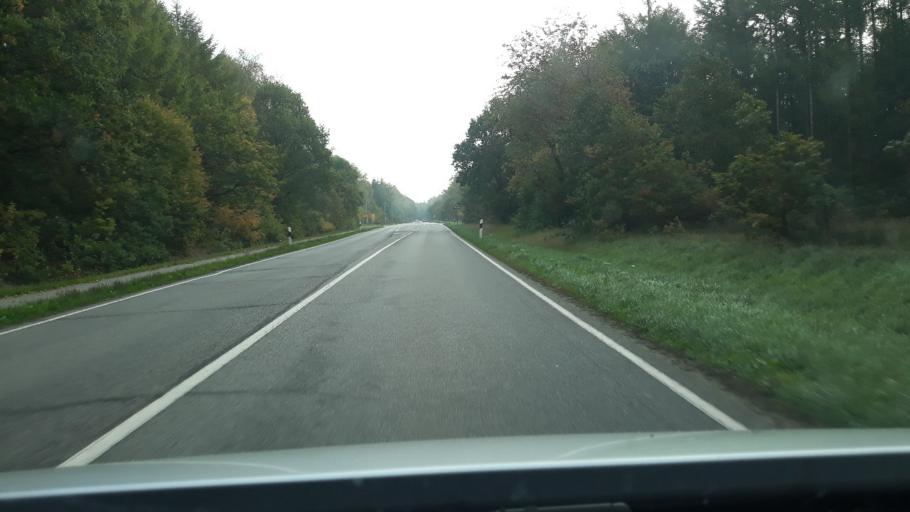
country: DE
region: Schleswig-Holstein
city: Kropp
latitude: 54.4033
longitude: 9.5088
